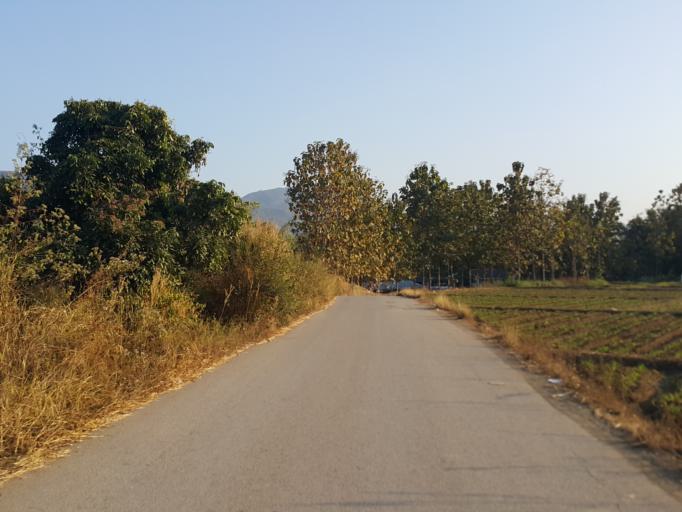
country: TH
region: Chiang Mai
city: Mae On
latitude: 18.7768
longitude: 99.2569
